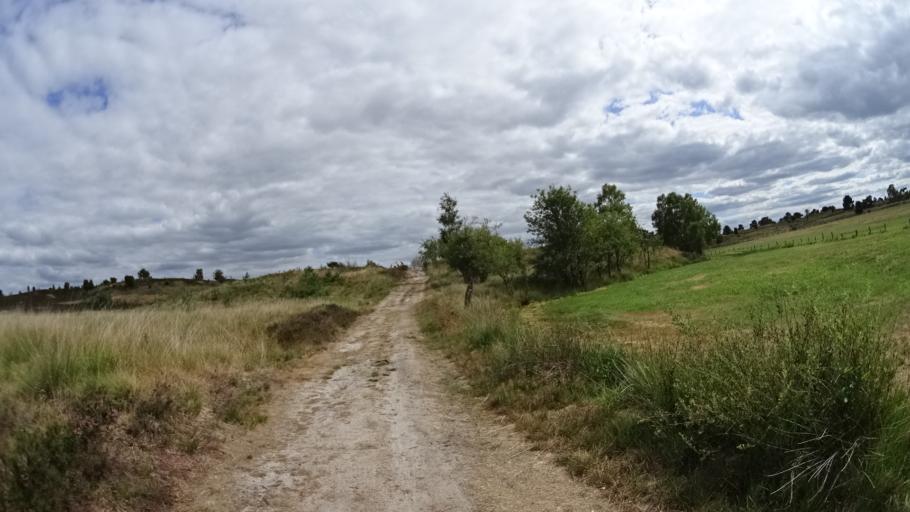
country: DE
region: Lower Saxony
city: Undeloh
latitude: 53.1868
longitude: 9.9917
